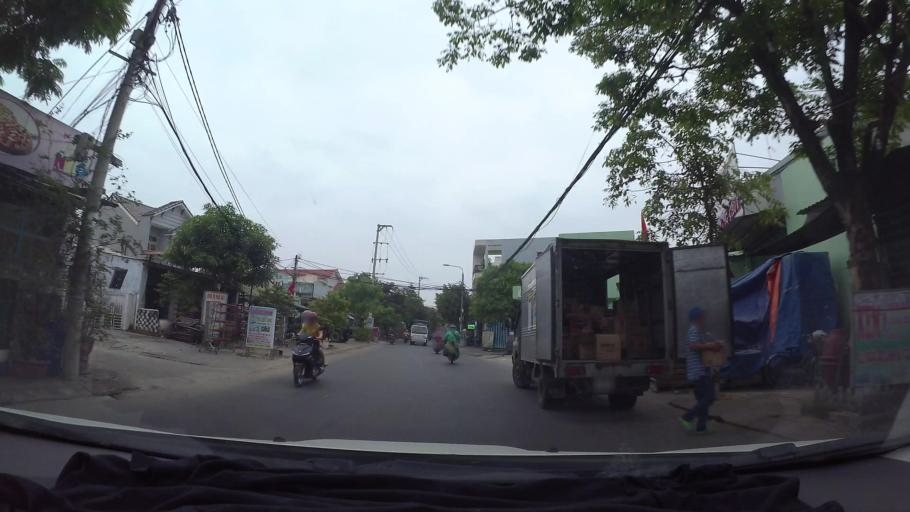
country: VN
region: Da Nang
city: Thanh Khe
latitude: 16.0499
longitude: 108.1806
